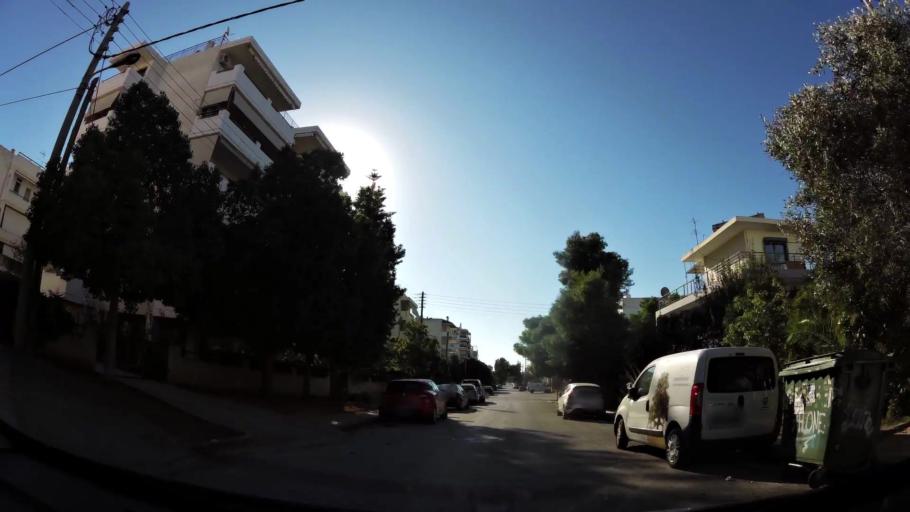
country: GR
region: Attica
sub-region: Nomarchia Athinas
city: Glyfada
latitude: 37.8679
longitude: 23.7609
